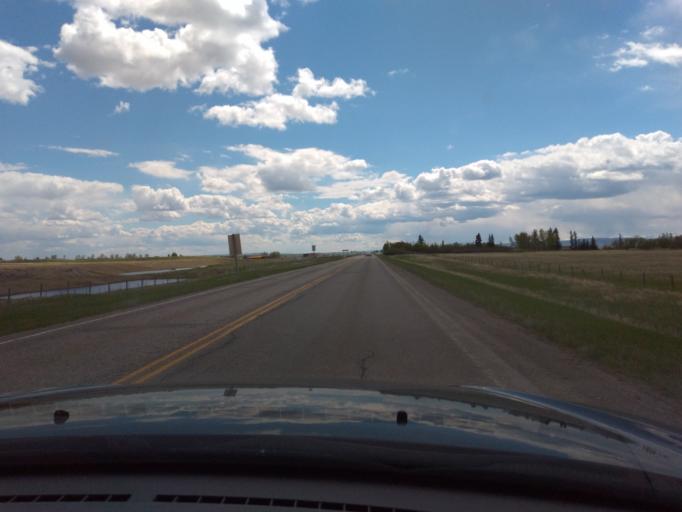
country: CA
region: Alberta
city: Cochrane
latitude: 51.0956
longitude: -114.3504
